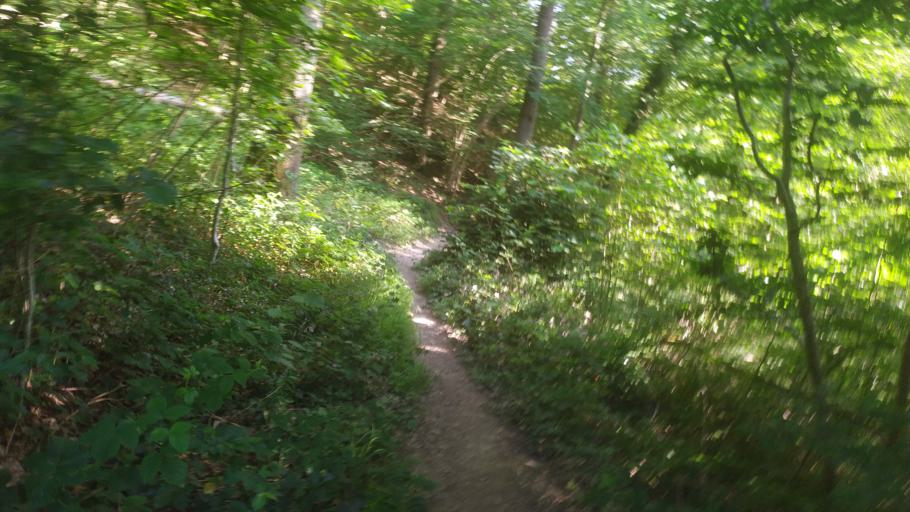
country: BE
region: Wallonia
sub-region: Province de Namur
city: Houyet
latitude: 50.2026
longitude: 4.9994
